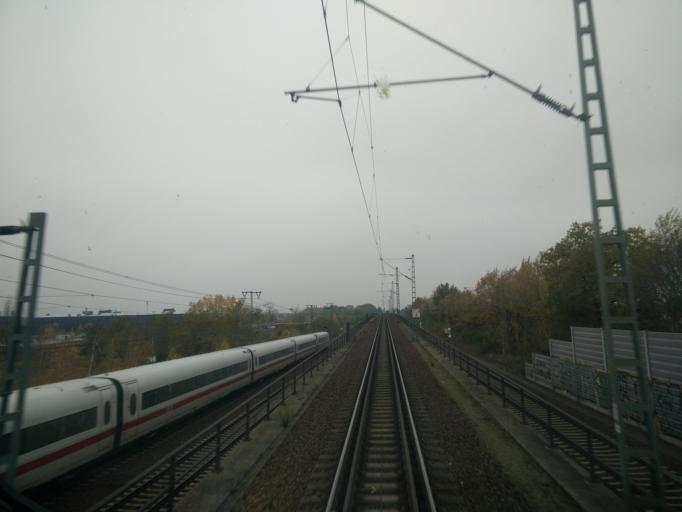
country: DE
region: Berlin
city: Wilhelmstadt
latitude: 52.5383
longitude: 13.1747
